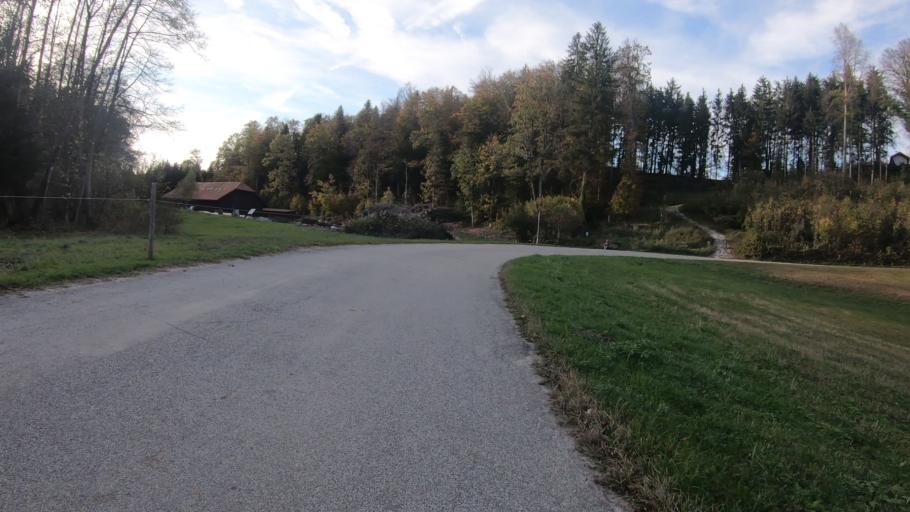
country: DE
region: Bavaria
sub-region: Upper Bavaria
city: Siegsdorf
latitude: 47.8106
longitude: 12.6203
